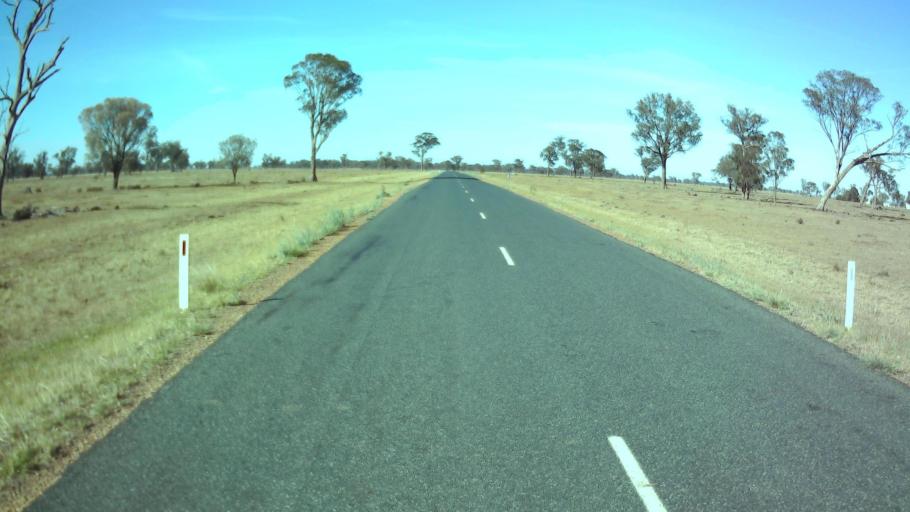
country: AU
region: New South Wales
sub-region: Weddin
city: Grenfell
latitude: -34.0462
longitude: 147.9242
